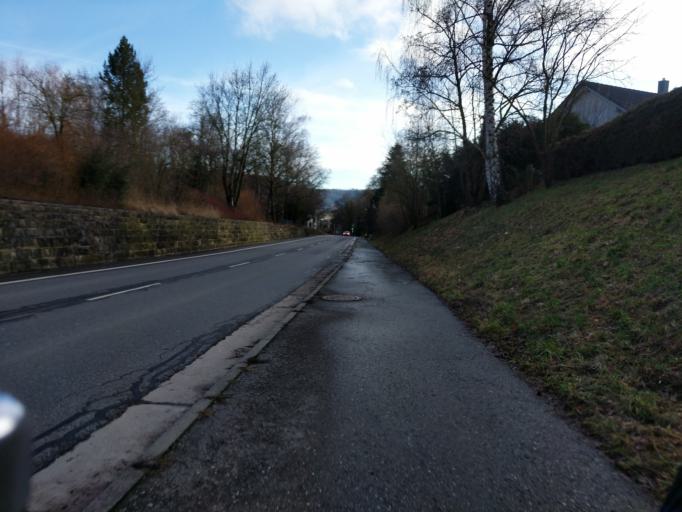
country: DE
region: Baden-Wuerttemberg
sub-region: Tuebingen Region
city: Rottenburg
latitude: 48.4832
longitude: 8.9361
